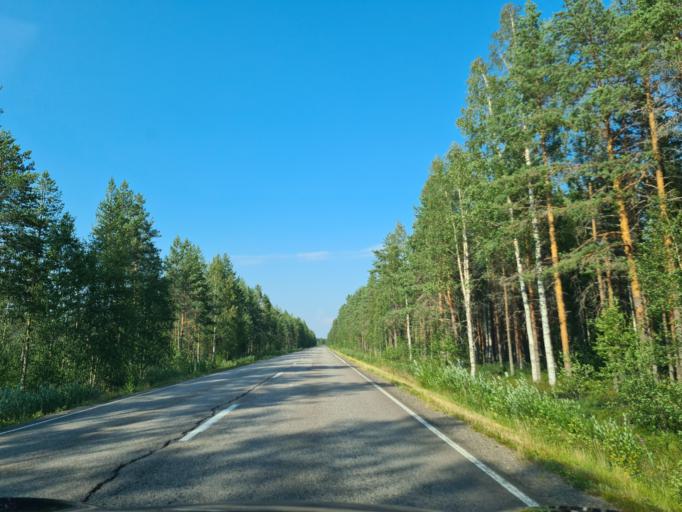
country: FI
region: Satakunta
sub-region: Pohjois-Satakunta
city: Karvia
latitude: 62.3059
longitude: 22.6437
